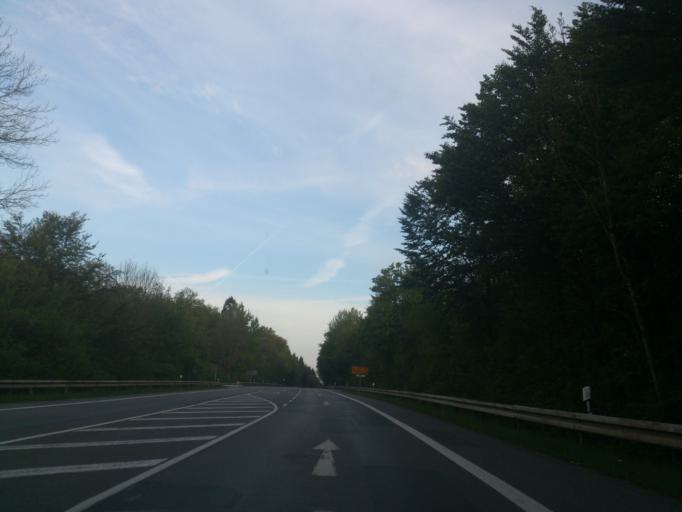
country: DE
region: North Rhine-Westphalia
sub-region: Regierungsbezirk Detmold
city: Bad Driburg
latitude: 51.6875
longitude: 8.9753
